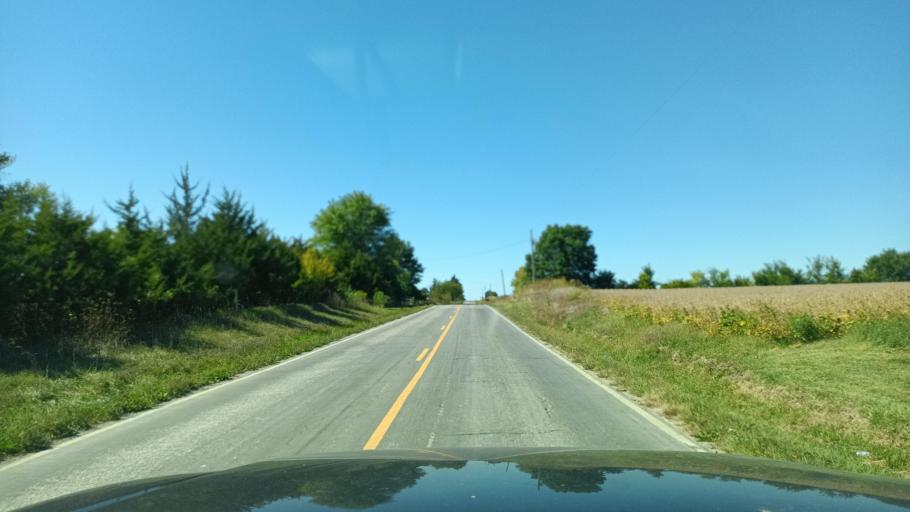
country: US
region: Missouri
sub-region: Macon County
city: La Plata
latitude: 40.0224
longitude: -92.5598
